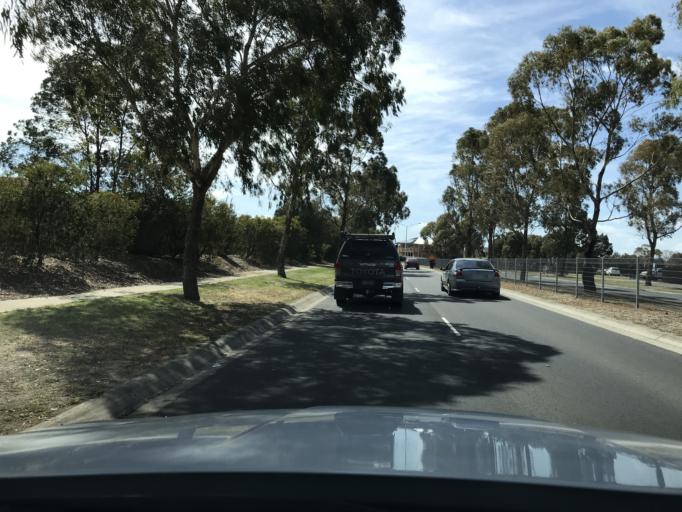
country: AU
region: Victoria
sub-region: Hume
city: Roxburgh Park
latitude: -37.6302
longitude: 144.9294
